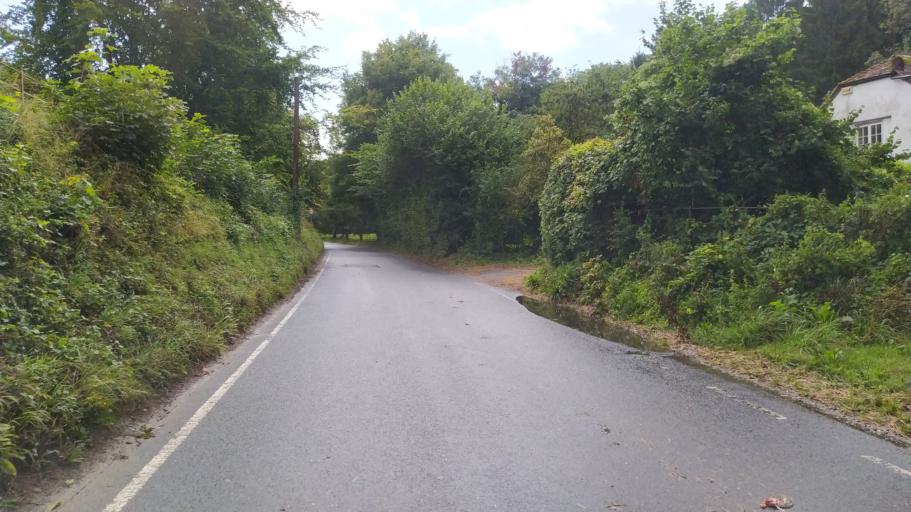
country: GB
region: England
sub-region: Wiltshire
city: Ansty
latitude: 50.9574
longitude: -2.0779
